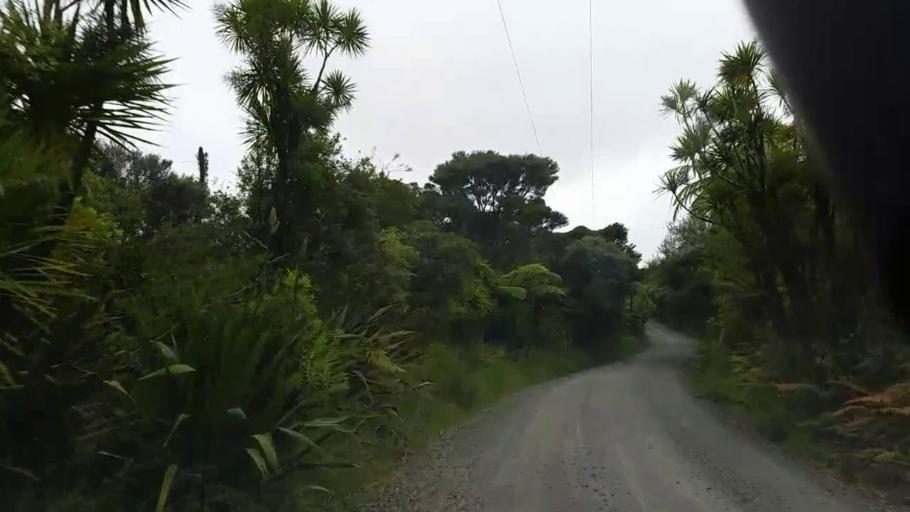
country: NZ
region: Auckland
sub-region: Auckland
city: Muriwai Beach
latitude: -36.9306
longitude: 174.5040
